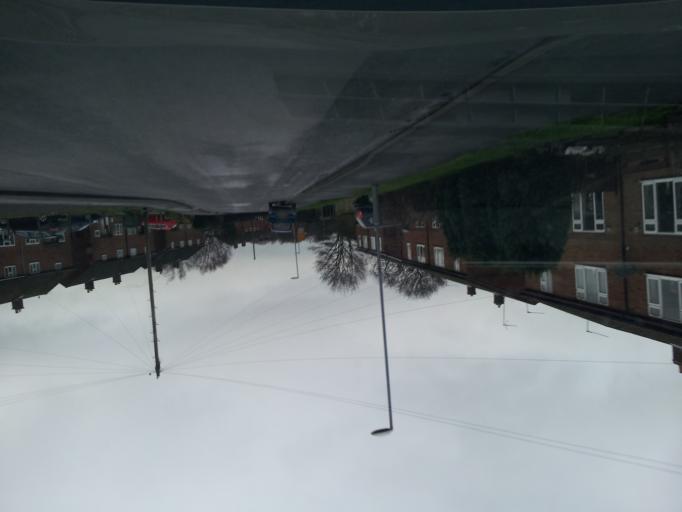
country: GB
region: England
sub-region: Leicestershire
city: Donisthorpe
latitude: 52.7466
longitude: -1.5167
